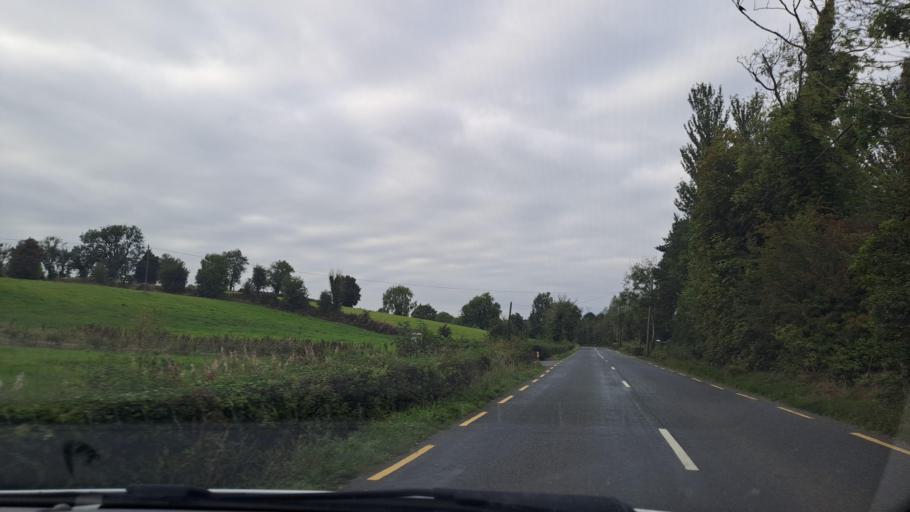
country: IE
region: Ulster
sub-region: County Monaghan
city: Carrickmacross
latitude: 54.0136
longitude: -6.7579
